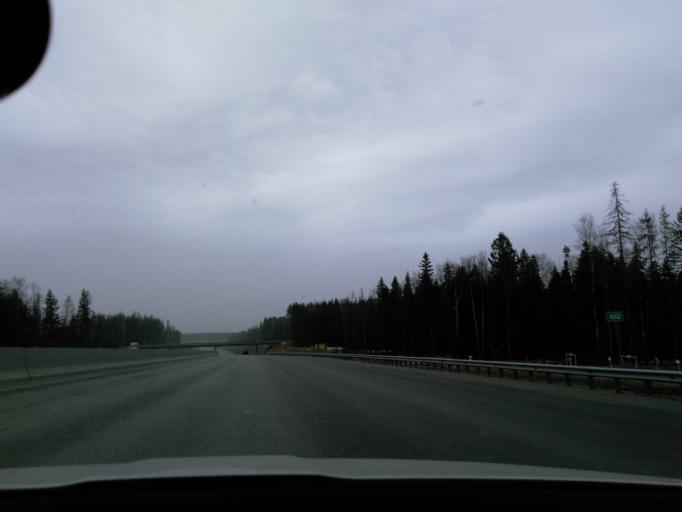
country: RU
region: Moskovskaya
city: Skhodnya
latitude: 55.9845
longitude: 37.3090
